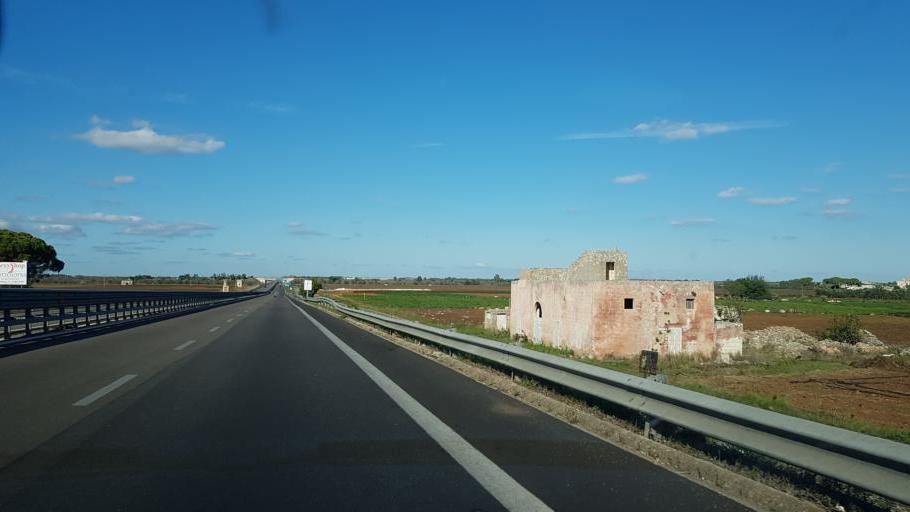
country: IT
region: Apulia
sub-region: Provincia di Lecce
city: Collemeto
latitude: 40.2486
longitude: 18.1147
